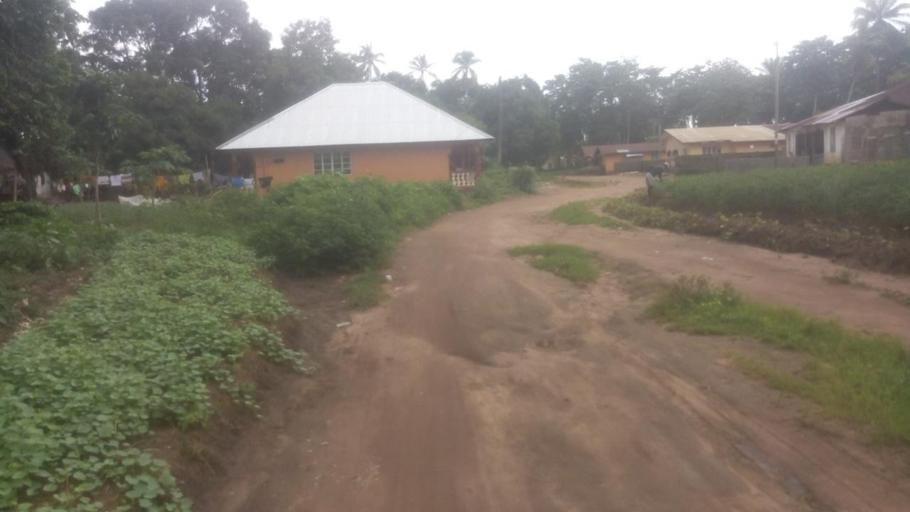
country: SL
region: Northern Province
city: Tintafor
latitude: 8.6427
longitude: -13.2244
